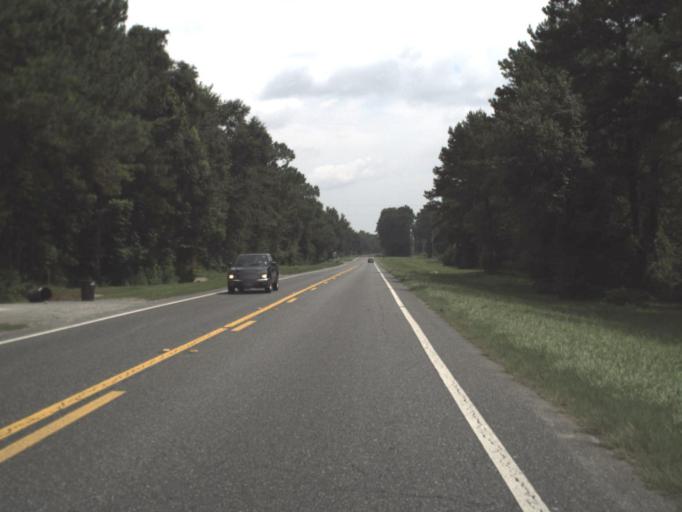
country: US
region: Florida
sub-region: Alachua County
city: High Springs
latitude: 29.9549
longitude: -82.6047
